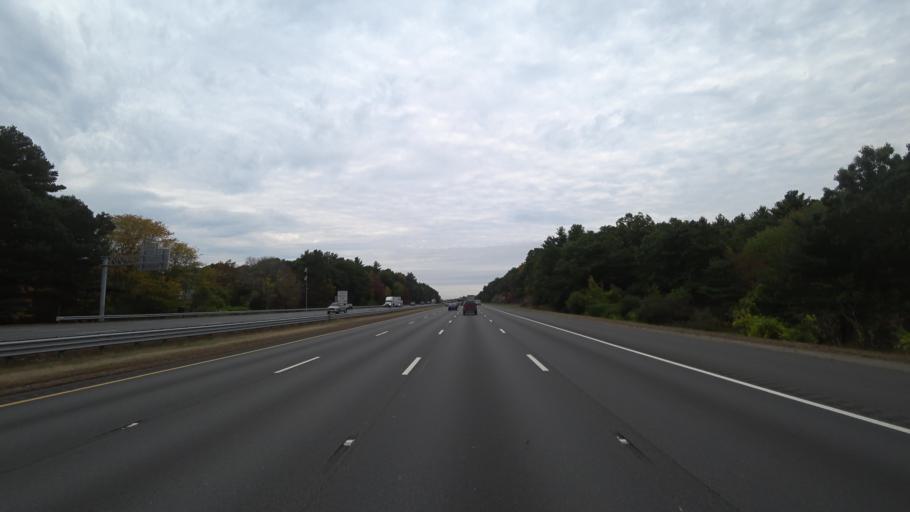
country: US
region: Massachusetts
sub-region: Middlesex County
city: Wilmington
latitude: 42.5645
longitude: -71.1439
